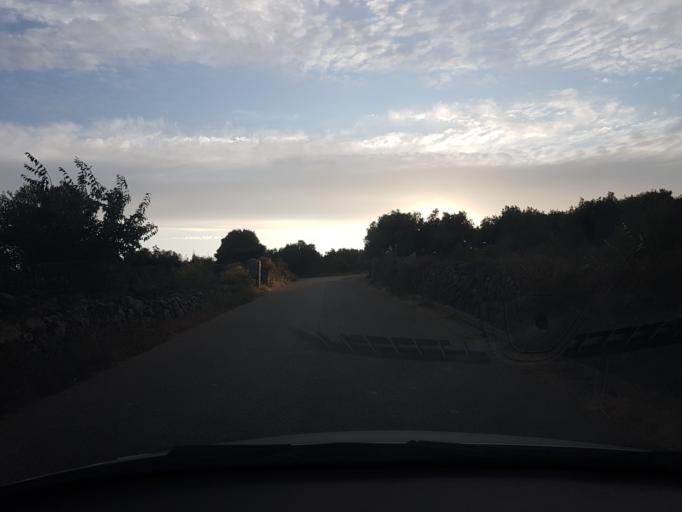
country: IT
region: Sardinia
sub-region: Provincia di Oristano
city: Seneghe
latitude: 40.0985
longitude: 8.6233
